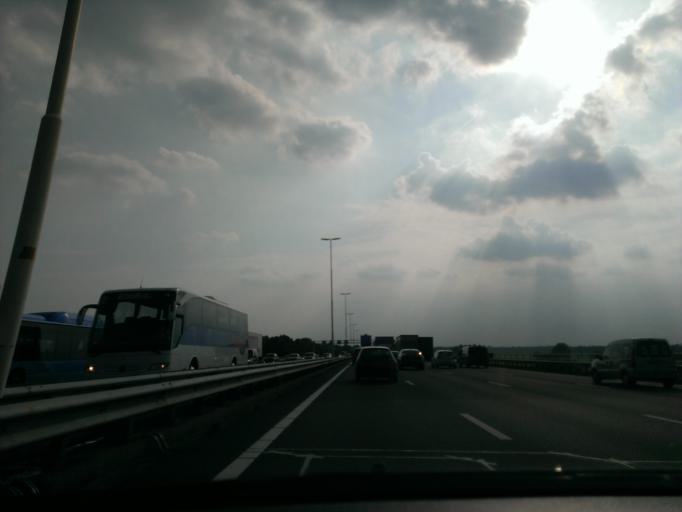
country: NL
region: Gelderland
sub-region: Gemeente Hattem
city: Hattem
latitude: 52.4989
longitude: 6.0525
